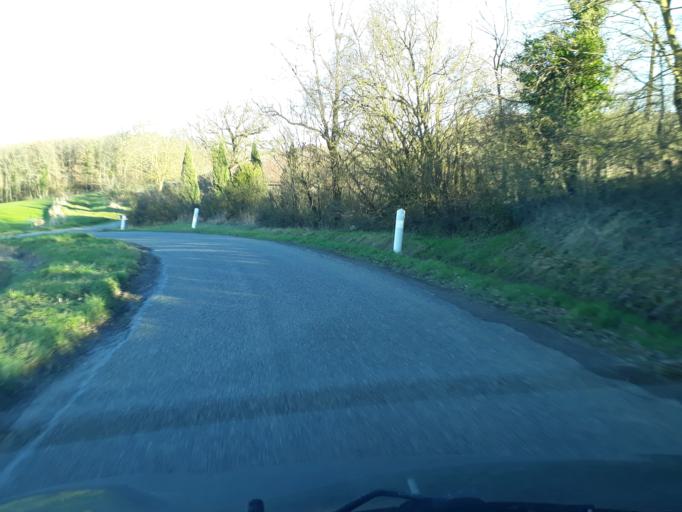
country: FR
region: Midi-Pyrenees
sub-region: Departement du Gers
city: Aubiet
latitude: 43.6399
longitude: 0.7013
